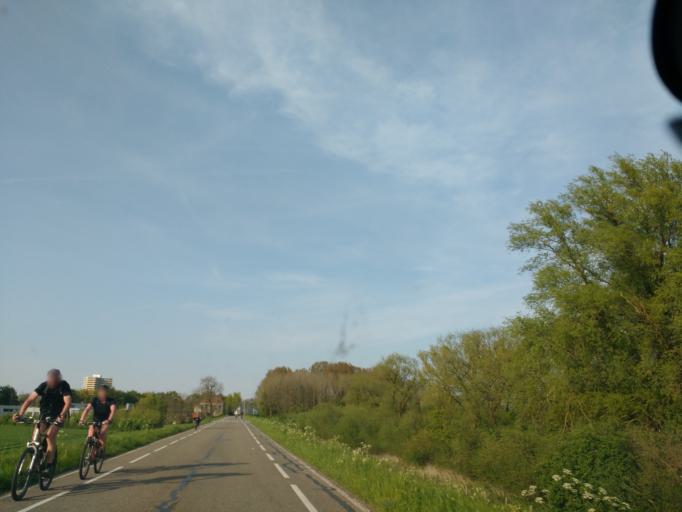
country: NL
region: Gelderland
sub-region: Gemeente Wageningen
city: Wageningen
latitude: 51.9541
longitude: 5.6426
